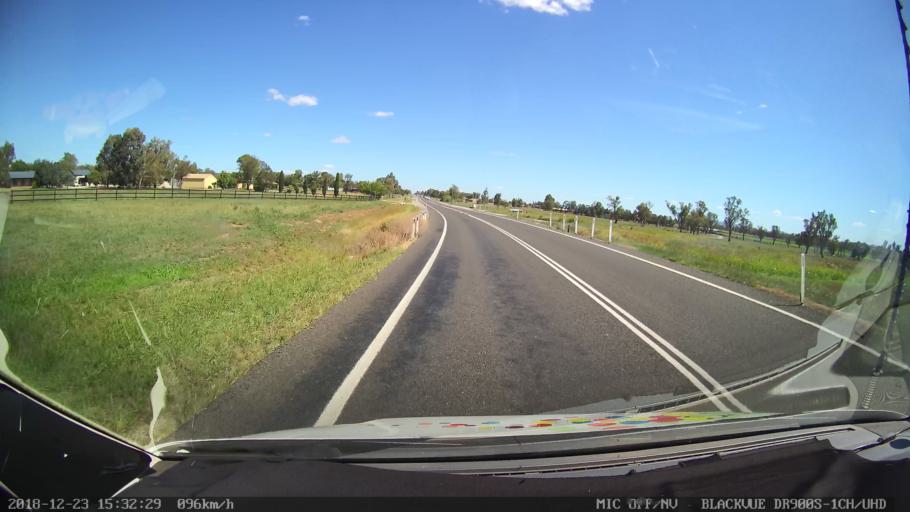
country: AU
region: New South Wales
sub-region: Tamworth Municipality
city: Tamworth
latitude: -30.9864
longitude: 150.8702
